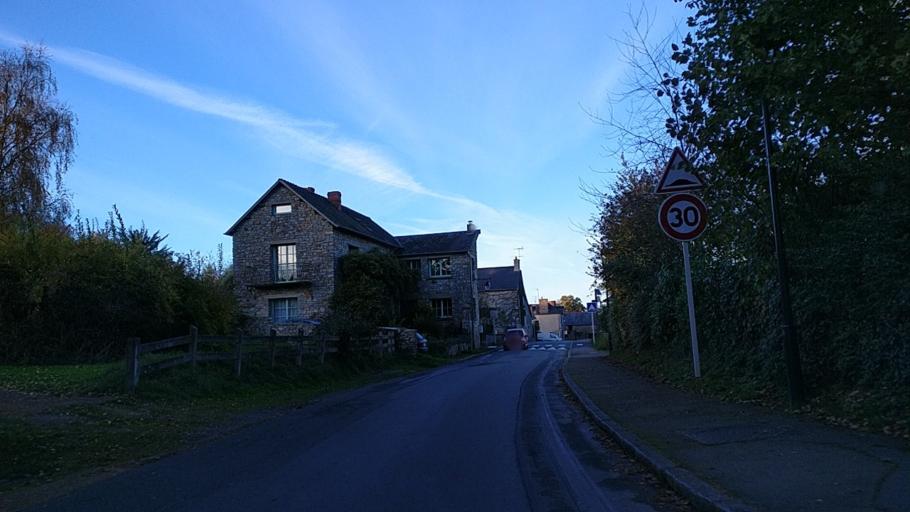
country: FR
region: Brittany
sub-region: Departement d'Ille-et-Vilaine
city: Saint-Sulpice-la-Foret
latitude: 48.2166
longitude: -1.5791
